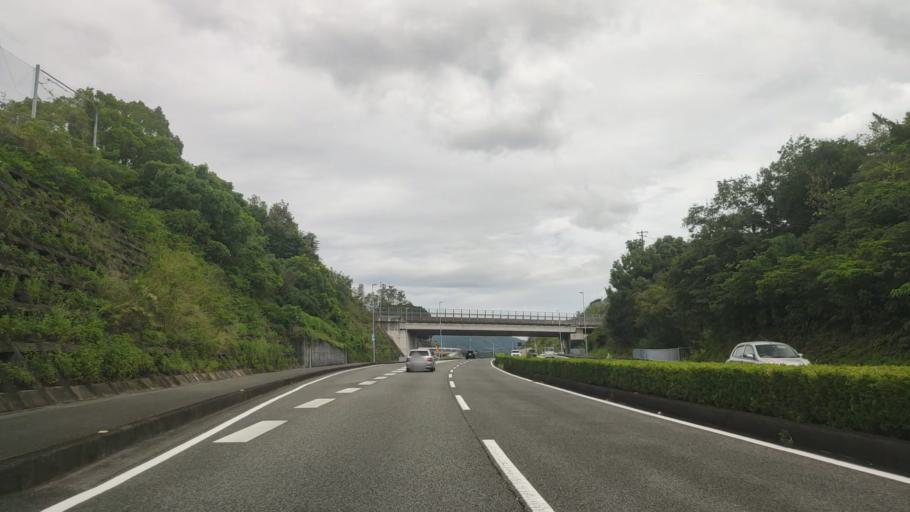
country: JP
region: Wakayama
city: Tanabe
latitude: 33.7310
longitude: 135.4004
